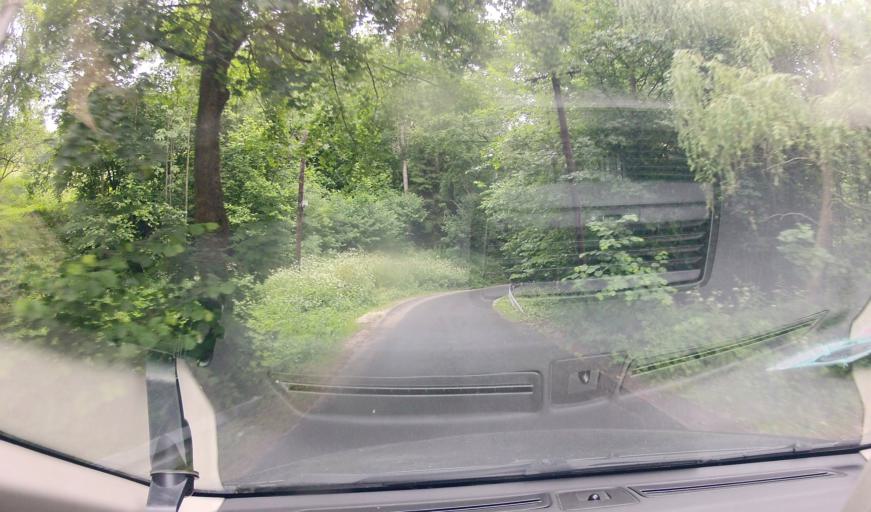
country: PL
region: Lower Silesian Voivodeship
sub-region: Powiat klodzki
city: Miedzylesie
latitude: 50.1186
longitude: 16.6522
